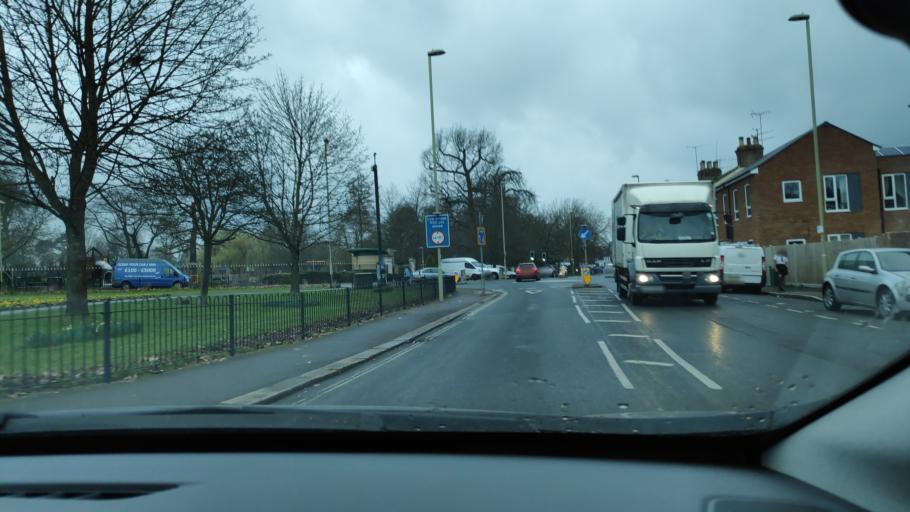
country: GB
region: England
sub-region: Hampshire
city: Aldershot
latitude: 51.2431
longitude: -0.7520
